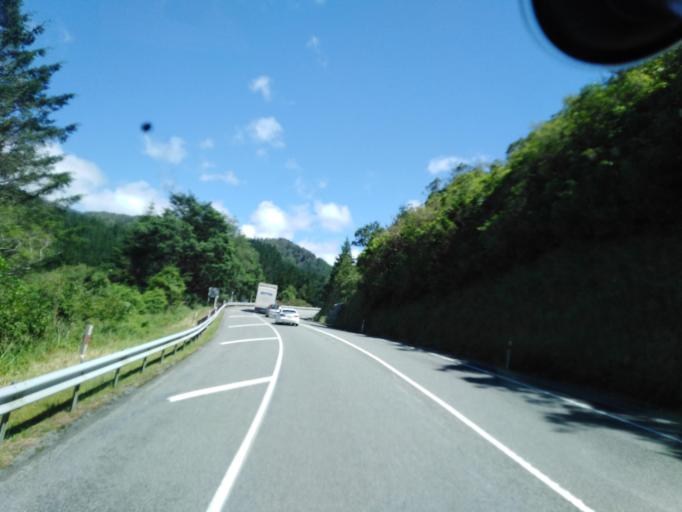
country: NZ
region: Nelson
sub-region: Nelson City
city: Nelson
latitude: -41.1977
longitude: 173.5598
